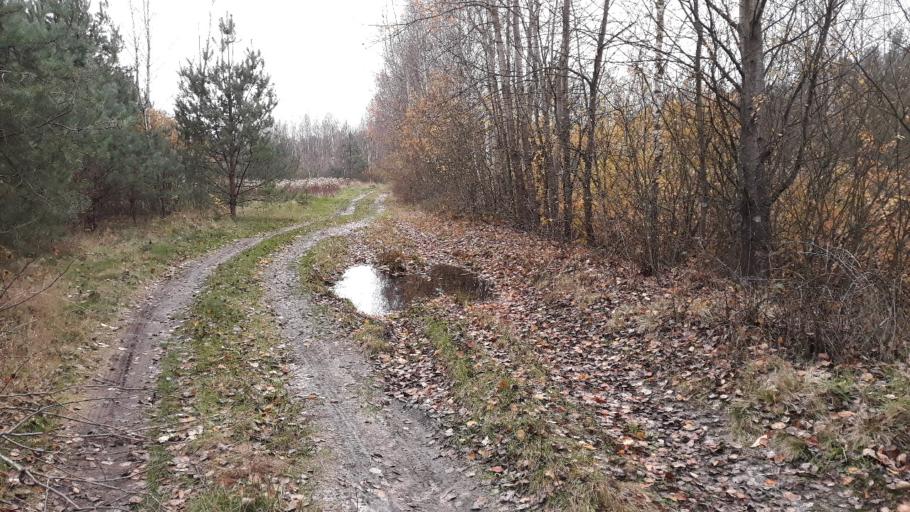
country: PL
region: Lublin Voivodeship
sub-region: Powiat janowski
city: Dzwola
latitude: 50.6498
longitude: 22.5719
